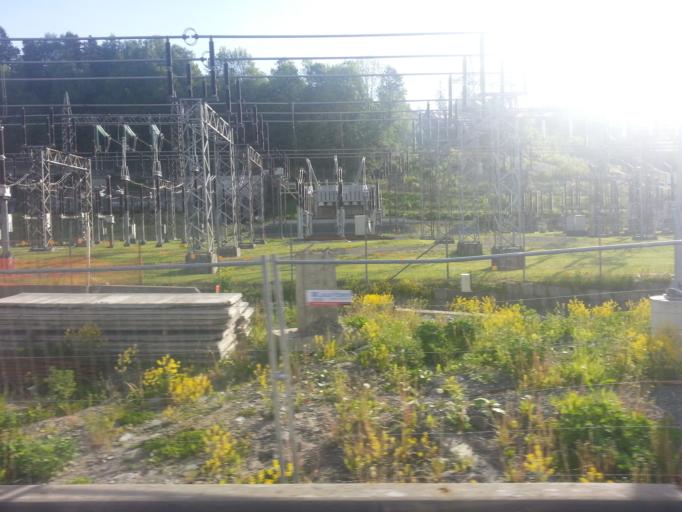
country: NO
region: Akershus
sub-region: Asker
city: Billingstad
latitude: 59.8975
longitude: 10.4992
